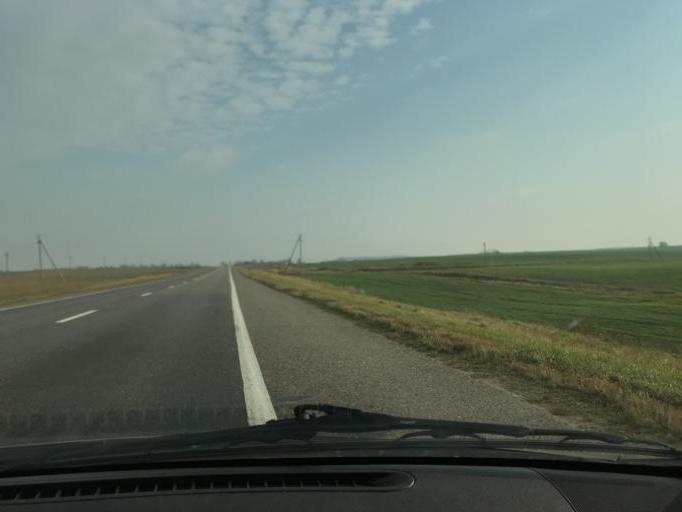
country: BY
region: Vitebsk
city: Chashniki
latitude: 55.0135
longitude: 28.9989
